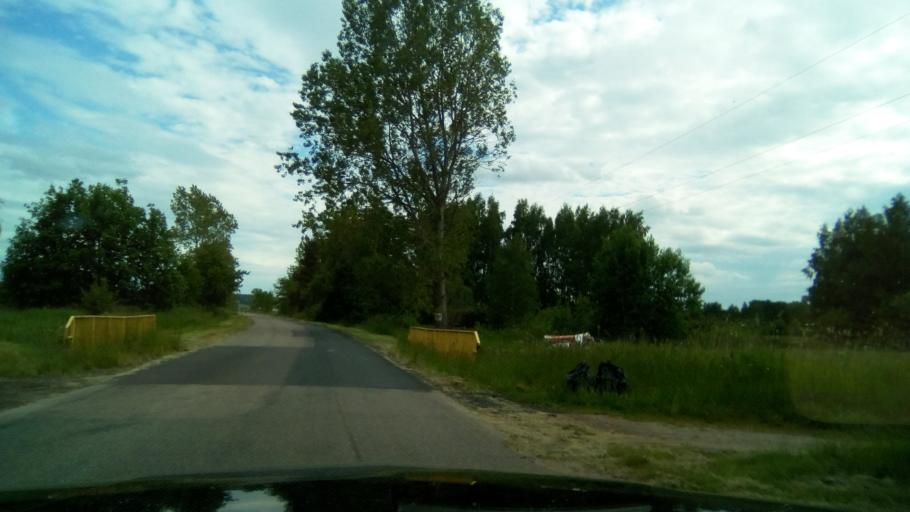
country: PL
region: Pomeranian Voivodeship
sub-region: Powiat pucki
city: Krokowa
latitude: 54.8206
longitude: 18.0869
